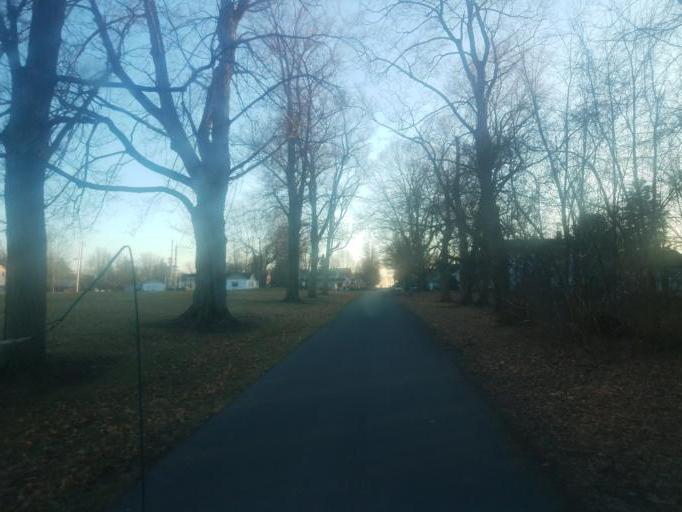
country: US
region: Ohio
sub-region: Wyandot County
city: Upper Sandusky
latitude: 40.8158
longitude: -83.1341
